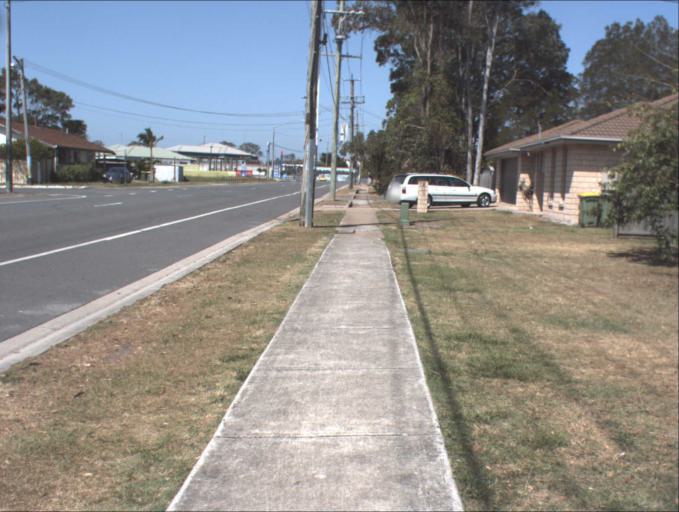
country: AU
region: Queensland
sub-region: Logan
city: Beenleigh
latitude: -27.6906
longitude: 153.1888
